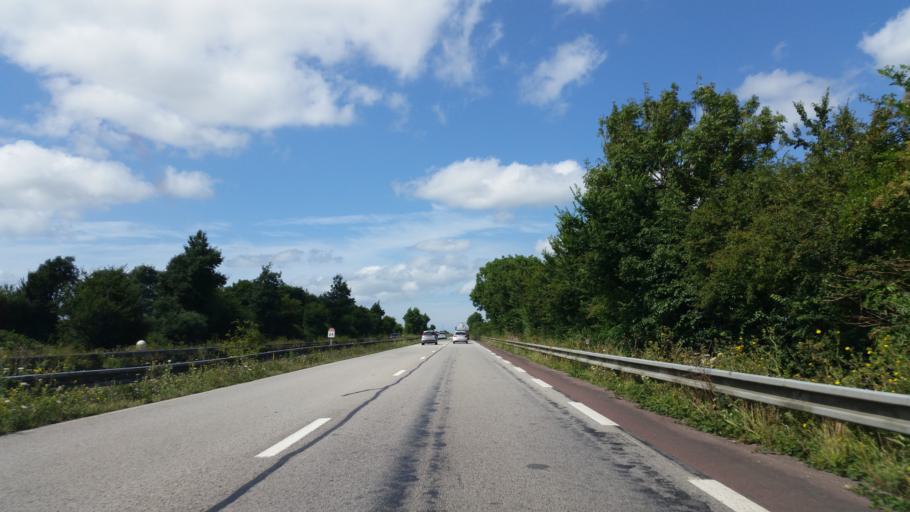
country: FR
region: Lower Normandy
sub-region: Departement de la Manche
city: Sainte-Mere-Eglise
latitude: 49.4331
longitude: -1.3365
